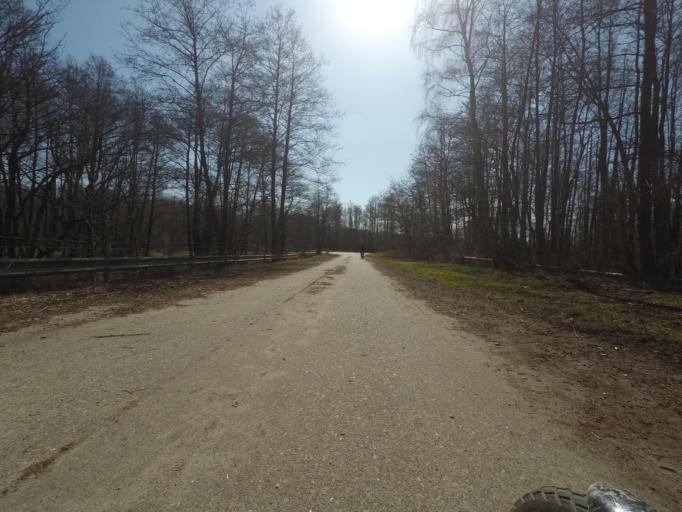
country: DE
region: Schleswig-Holstein
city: Stapelfeld
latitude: 53.6238
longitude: 10.1975
